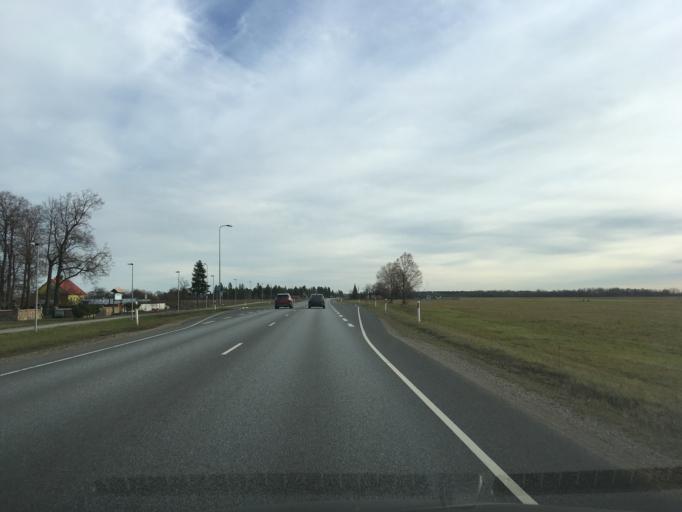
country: EE
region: Ida-Virumaa
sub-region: Narva linn
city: Narva
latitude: 59.3902
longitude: 28.1046
